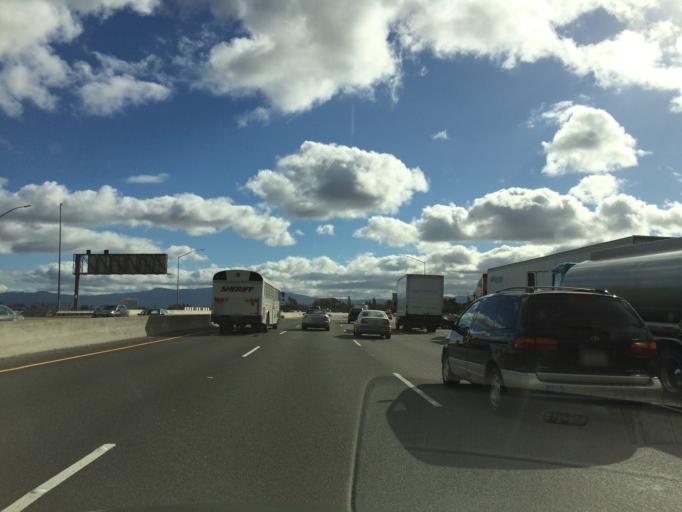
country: US
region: California
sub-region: Santa Clara County
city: San Jose
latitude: 37.3657
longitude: -121.9014
